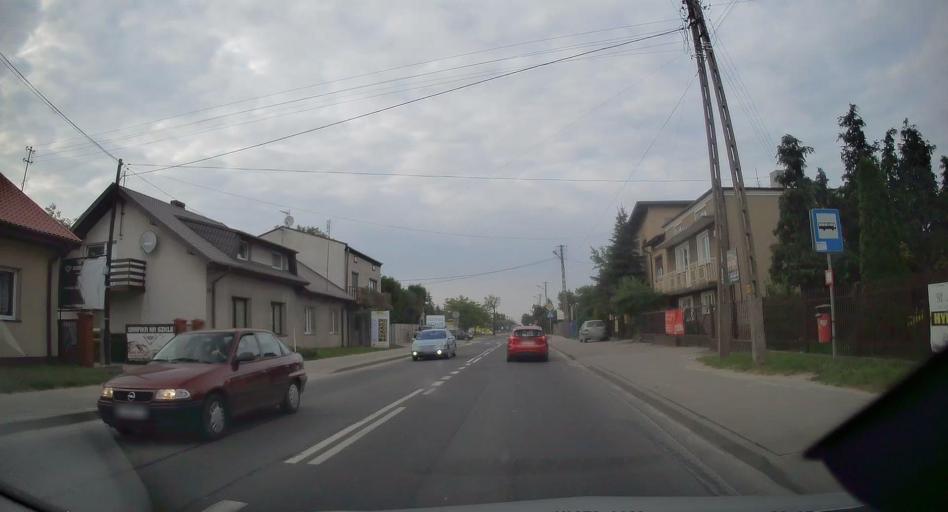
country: PL
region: Lodz Voivodeship
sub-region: Powiat radomszczanski
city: Radomsko
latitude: 51.0805
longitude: 19.4510
